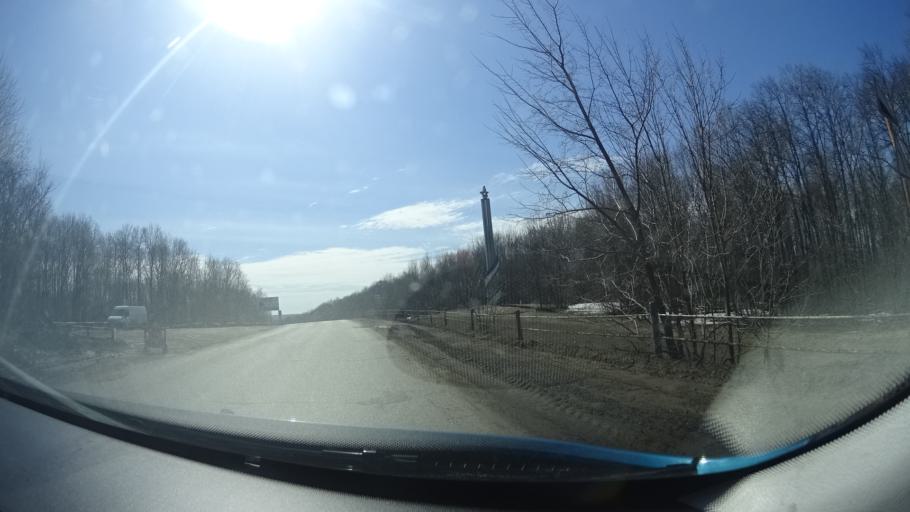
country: RU
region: Bashkortostan
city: Oktyabr'skiy
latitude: 54.4705
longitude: 53.5756
